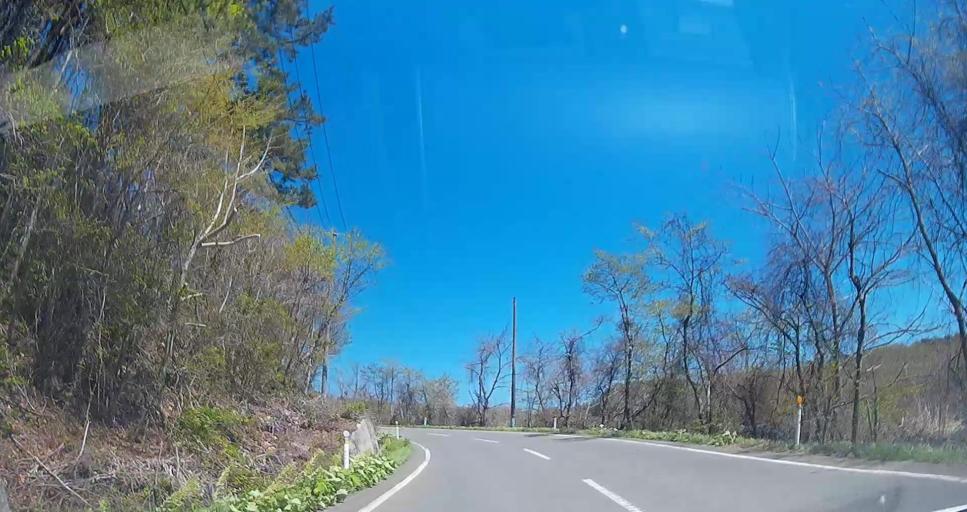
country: JP
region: Aomori
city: Mutsu
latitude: 41.2640
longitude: 141.3914
